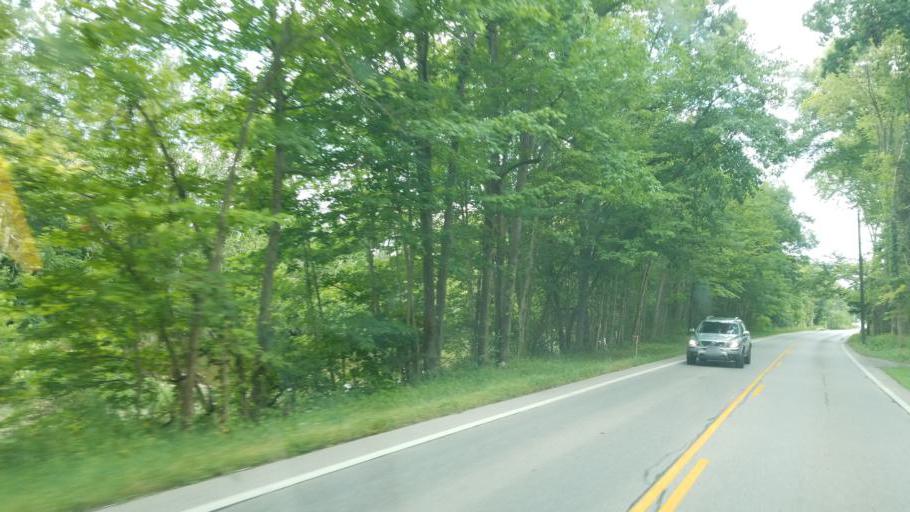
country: US
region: Ohio
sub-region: Delaware County
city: Powell
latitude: 40.1801
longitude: -83.0486
